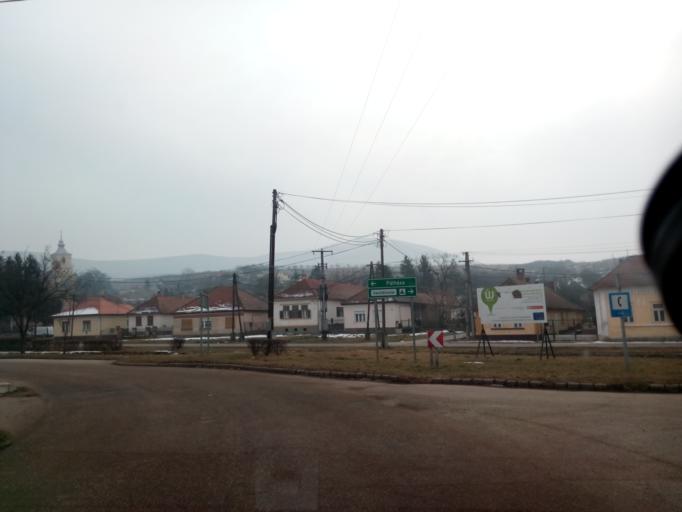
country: HU
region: Borsod-Abauj-Zemplen
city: Gonc
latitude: 48.4713
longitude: 21.2737
